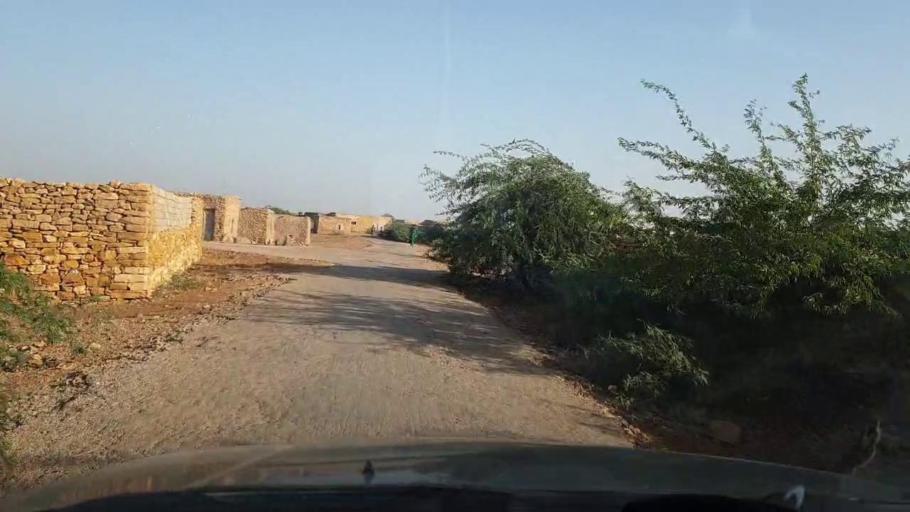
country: PK
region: Sindh
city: Kotri
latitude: 25.1322
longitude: 68.2304
